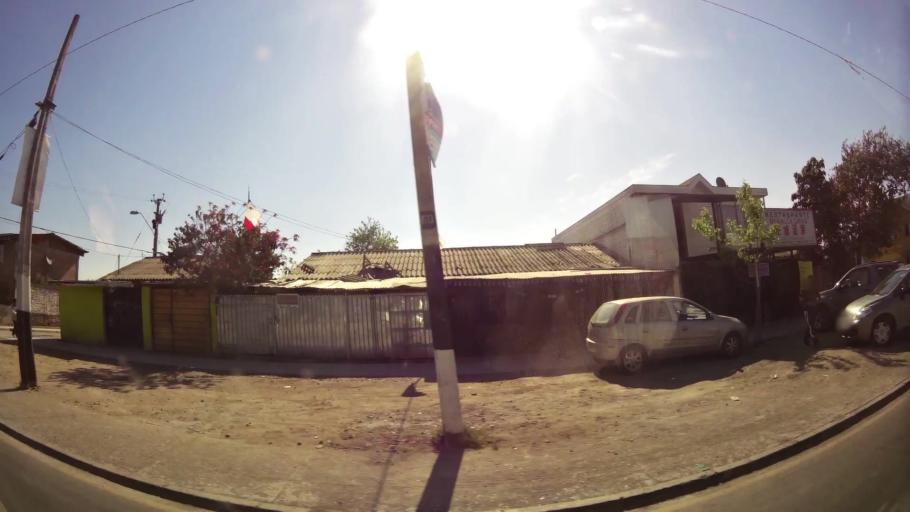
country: CL
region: Santiago Metropolitan
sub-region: Provincia de Santiago
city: Santiago
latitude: -33.5151
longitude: -70.6935
